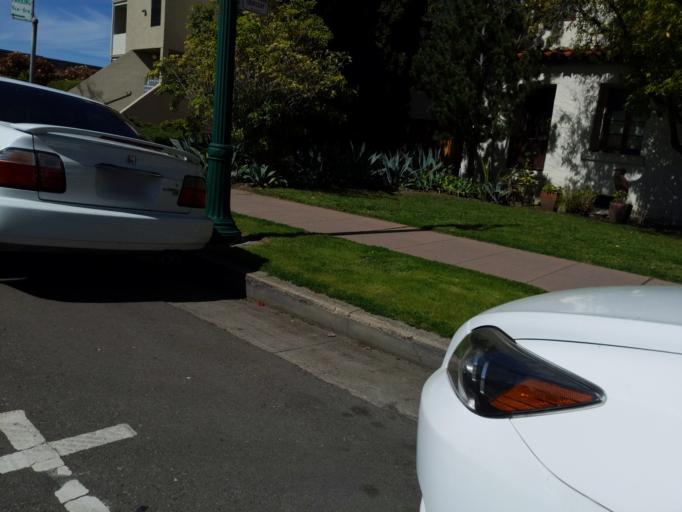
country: US
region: California
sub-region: Alameda County
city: Alameda
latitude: 37.7631
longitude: -122.2400
